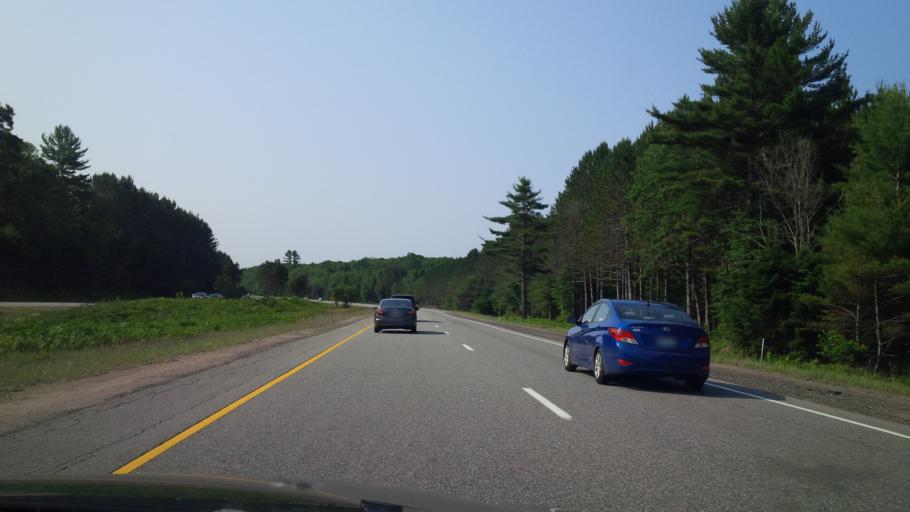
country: CA
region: Ontario
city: Bracebridge
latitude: 45.1084
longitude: -79.3109
